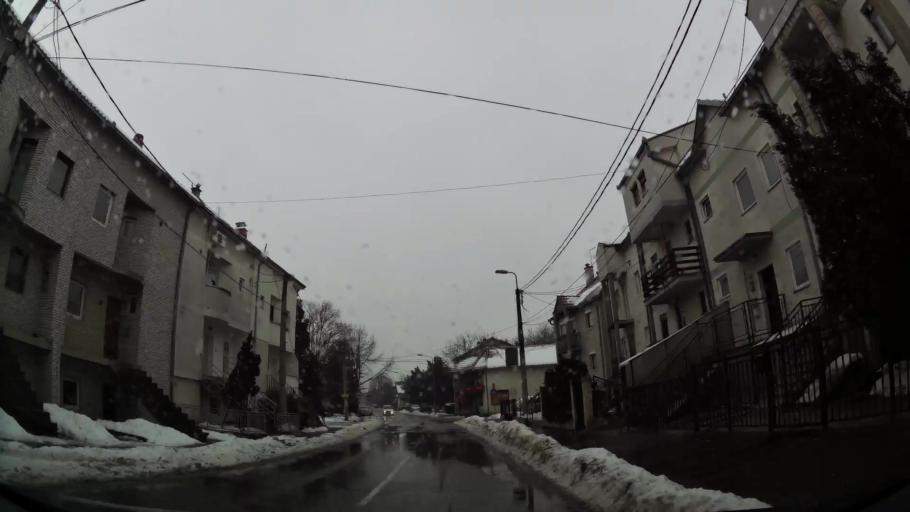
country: RS
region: Central Serbia
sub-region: Belgrade
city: Zemun
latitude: 44.8710
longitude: 20.3298
